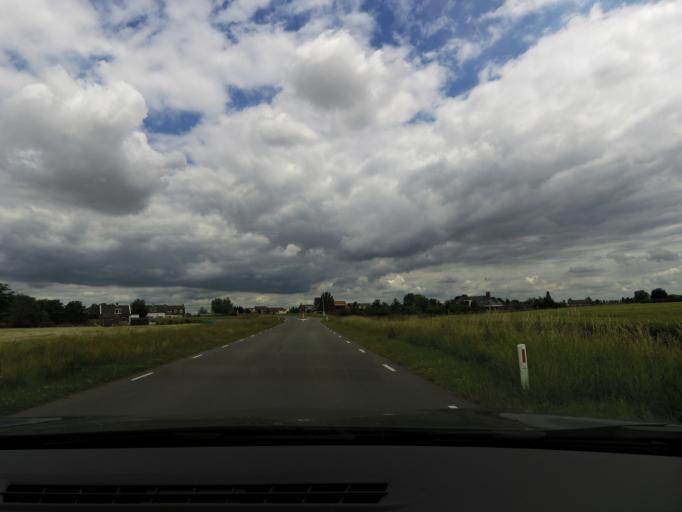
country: NL
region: South Holland
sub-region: Gemeente Strijen
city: Strijen
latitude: 51.7358
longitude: 4.5588
